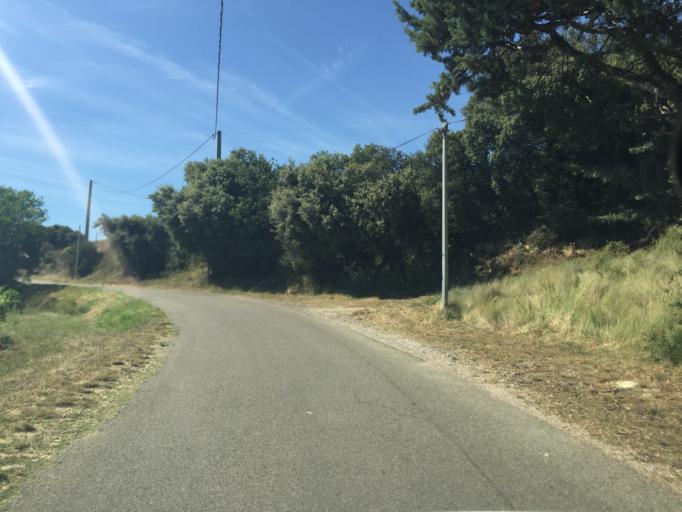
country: FR
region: Provence-Alpes-Cote d'Azur
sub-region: Departement du Vaucluse
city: Chateauneuf-du-Pape
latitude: 44.0597
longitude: 4.8145
